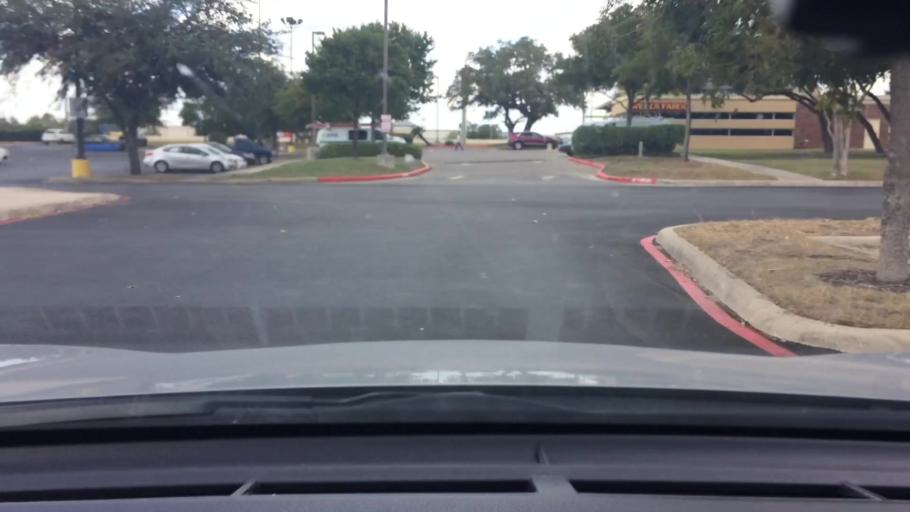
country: US
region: Texas
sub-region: Bexar County
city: Hollywood Park
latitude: 29.6055
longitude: -98.4605
